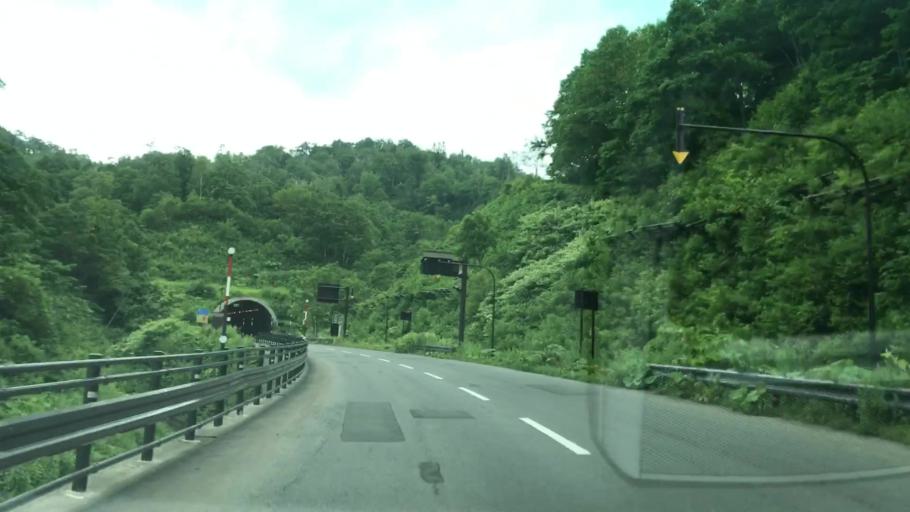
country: JP
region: Hokkaido
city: Yoichi
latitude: 42.9822
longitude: 140.8719
